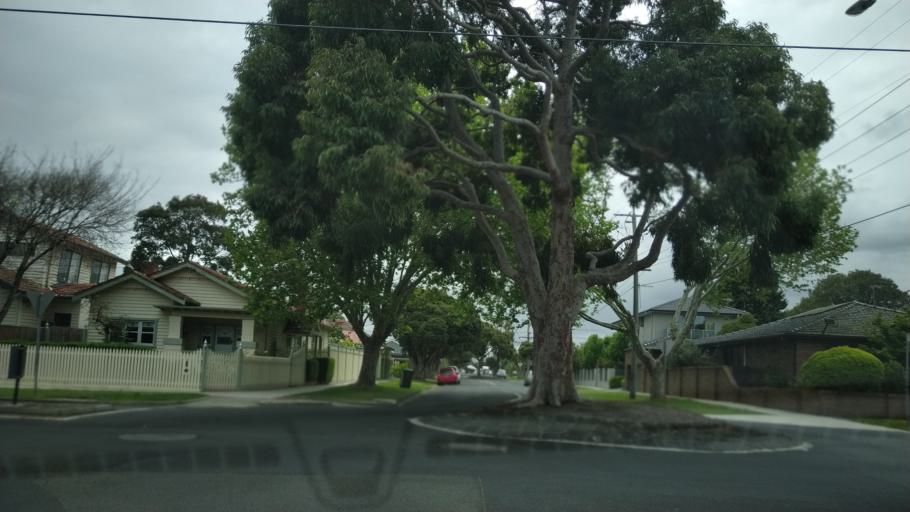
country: AU
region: Victoria
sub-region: Glen Eira
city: Caulfield South
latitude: -37.8910
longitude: 145.0233
